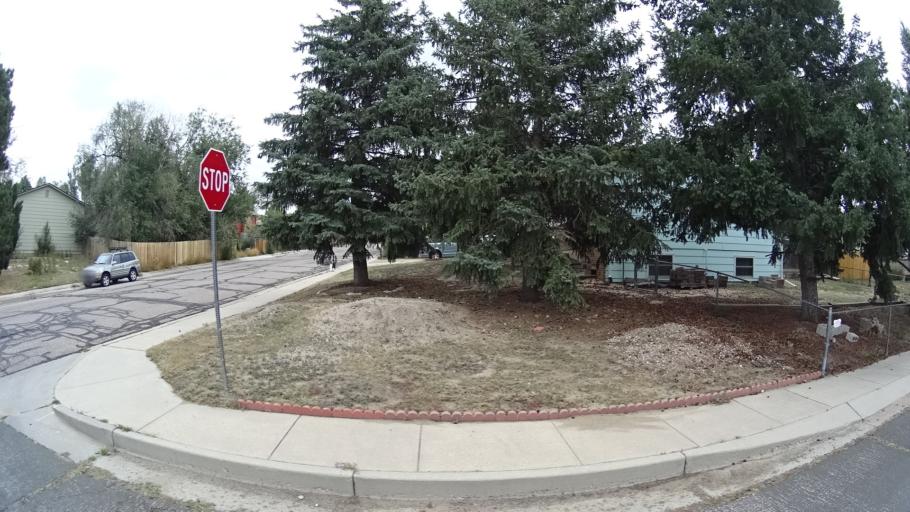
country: US
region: Colorado
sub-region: El Paso County
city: Cimarron Hills
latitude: 38.8902
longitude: -104.7359
